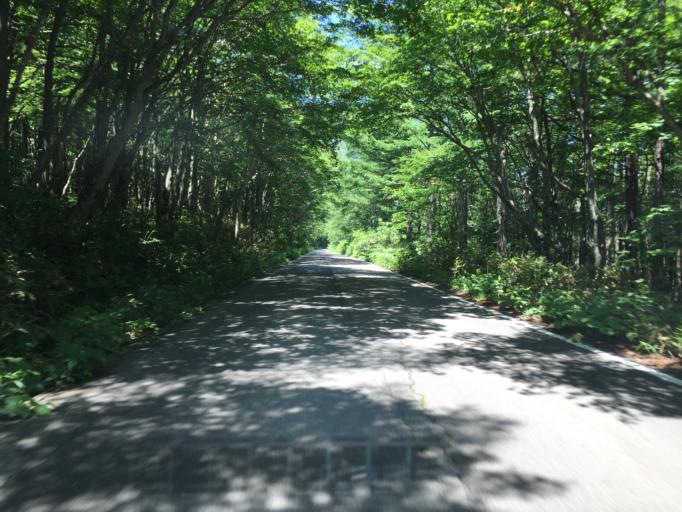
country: JP
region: Fukushima
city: Nihommatsu
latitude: 37.6575
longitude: 140.2904
